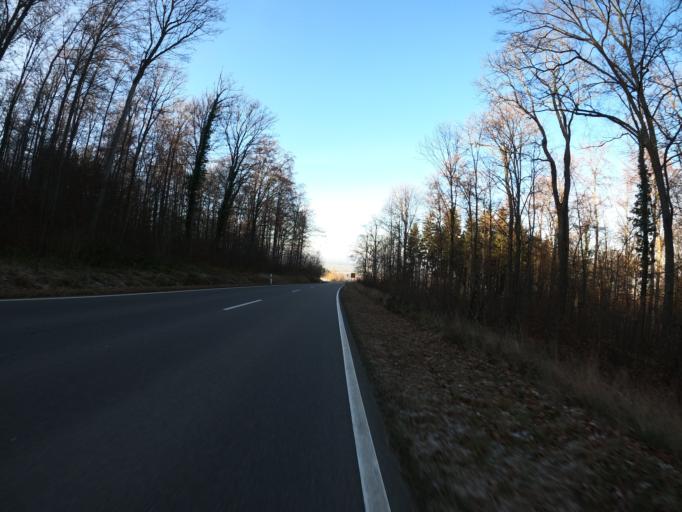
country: DE
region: Baden-Wuerttemberg
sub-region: Regierungsbezirk Stuttgart
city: Gammelshausen
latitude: 48.6324
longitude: 9.6609
